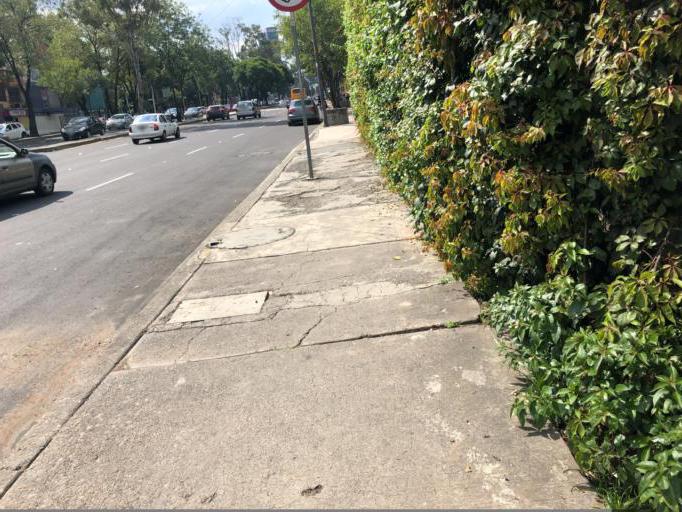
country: MX
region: Mexico City
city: Coyoacan
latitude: 19.3363
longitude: -99.1800
